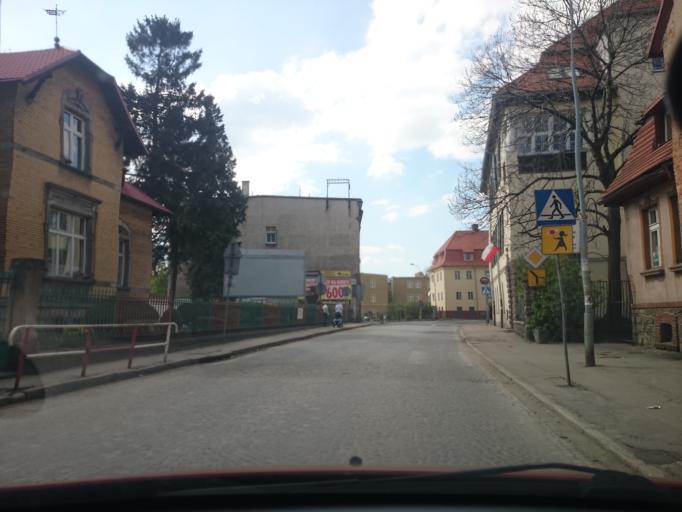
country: PL
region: Lower Silesian Voivodeship
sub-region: Powiat klodzki
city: Bystrzyca Klodzka
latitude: 50.2984
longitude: 16.6485
